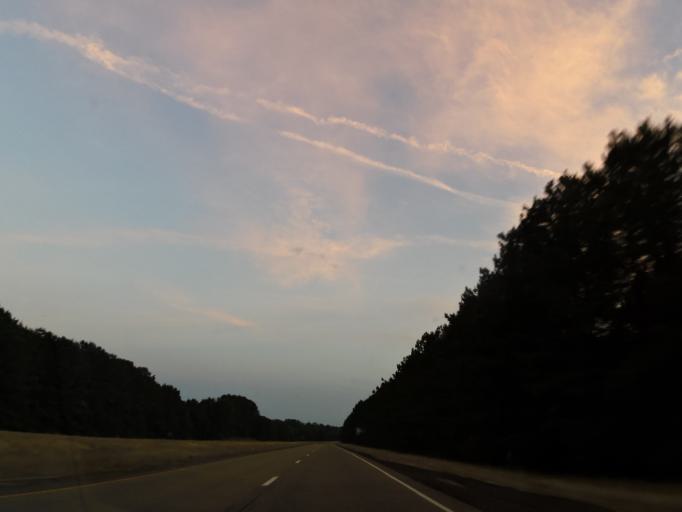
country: US
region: Mississippi
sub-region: Lauderdale County
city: Meridian Station
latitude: 32.6102
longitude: -88.4990
